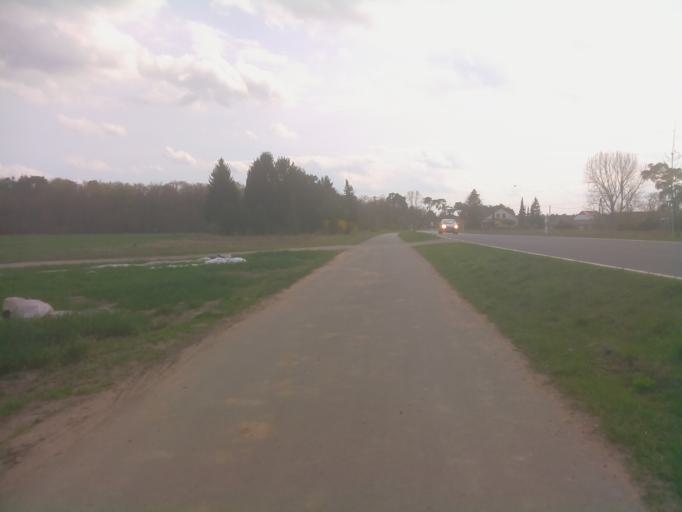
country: DE
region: Hesse
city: Lampertheim
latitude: 49.5761
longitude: 8.4941
